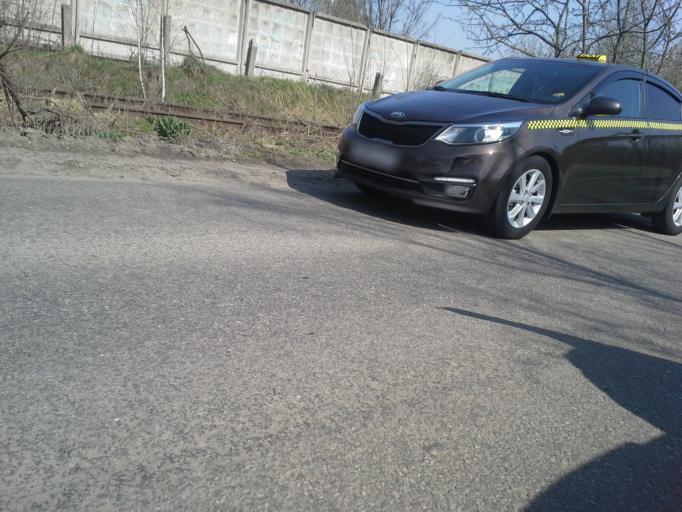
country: RU
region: Moskovskaya
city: Shcherbinka
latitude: 55.5115
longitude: 37.5481
